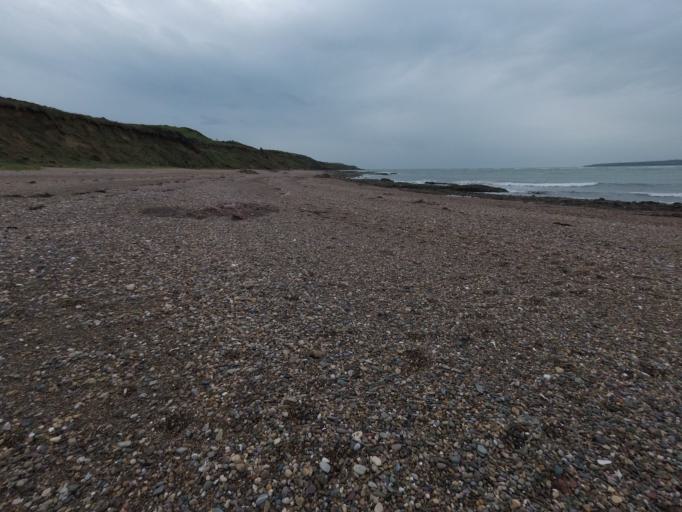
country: IE
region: Munster
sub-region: Waterford
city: Tra Mhor
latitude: 52.1438
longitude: -7.0913
